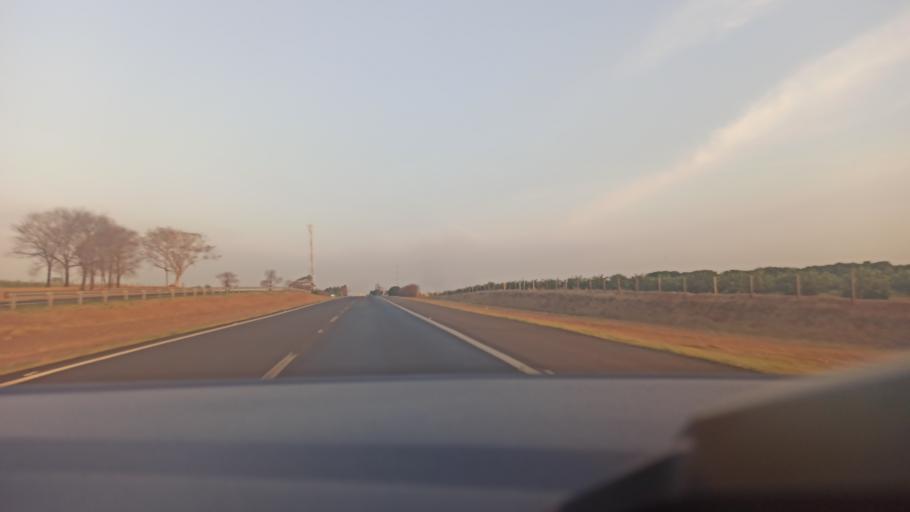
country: BR
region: Sao Paulo
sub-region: Santa Adelia
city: Santa Adelia
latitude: -21.4053
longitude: -48.6998
